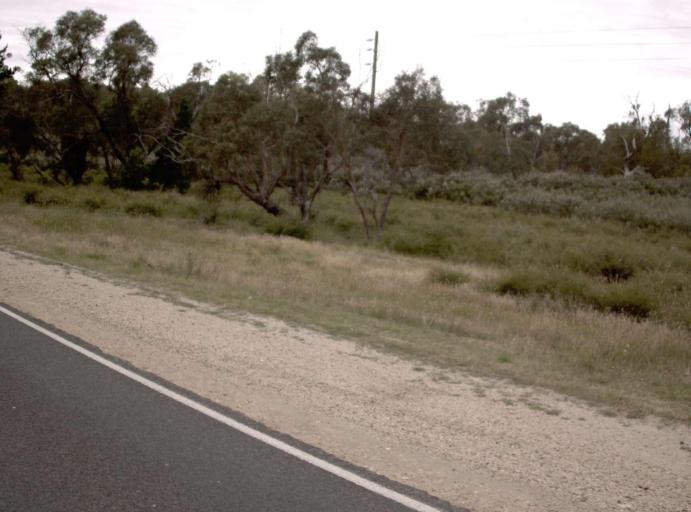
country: AU
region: Victoria
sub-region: Wellington
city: Sale
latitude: -38.1819
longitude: 147.1406
